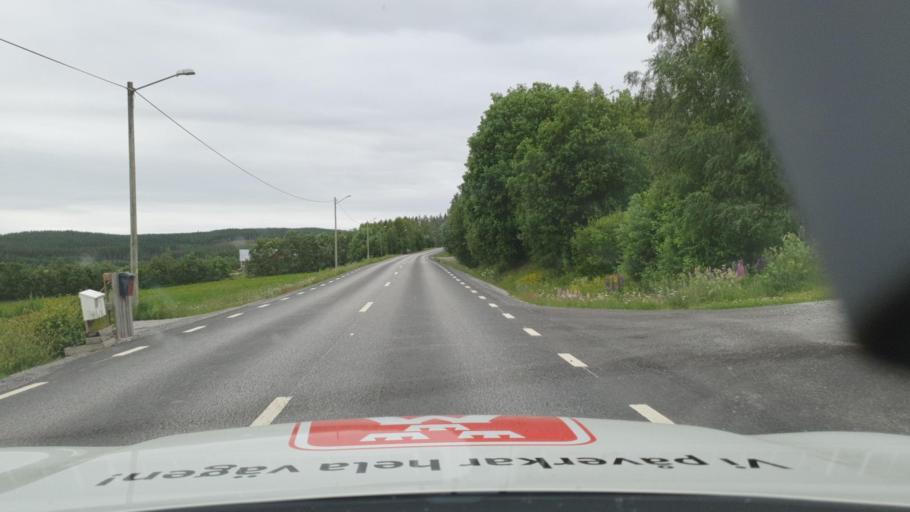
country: SE
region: Vaesterbotten
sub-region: Vannas Kommun
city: Vaennaes
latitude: 63.7388
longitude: 19.6526
